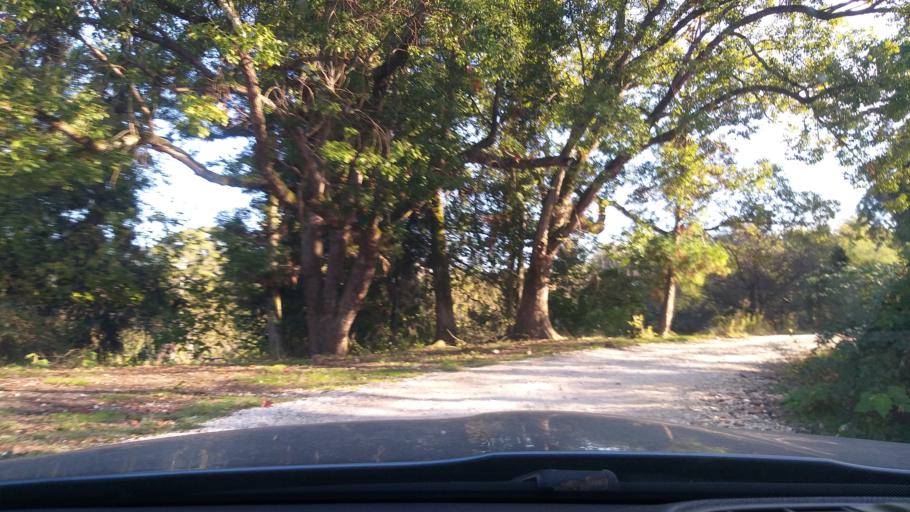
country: GE
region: Abkhazia
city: Stantsiya Novyy Afon
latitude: 43.0493
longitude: 40.9003
